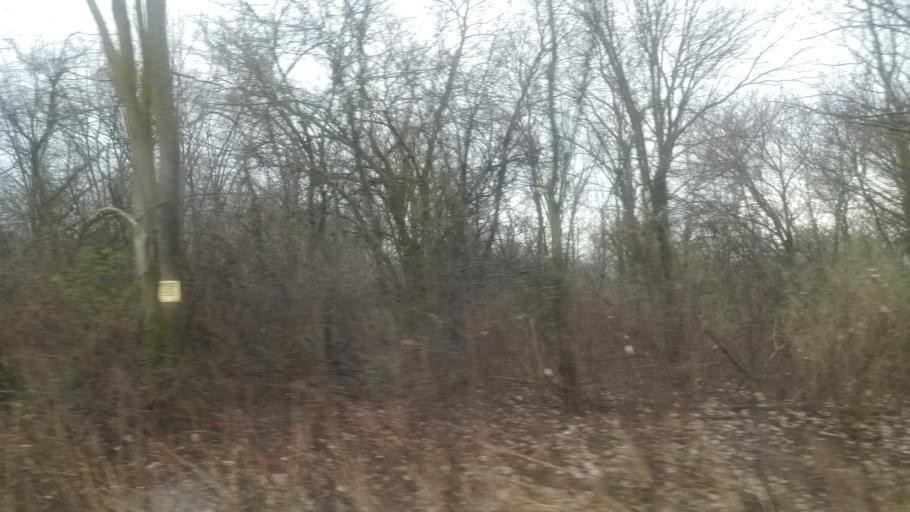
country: US
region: Ohio
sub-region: Wood County
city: Bowling Green
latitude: 41.3636
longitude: -83.6322
